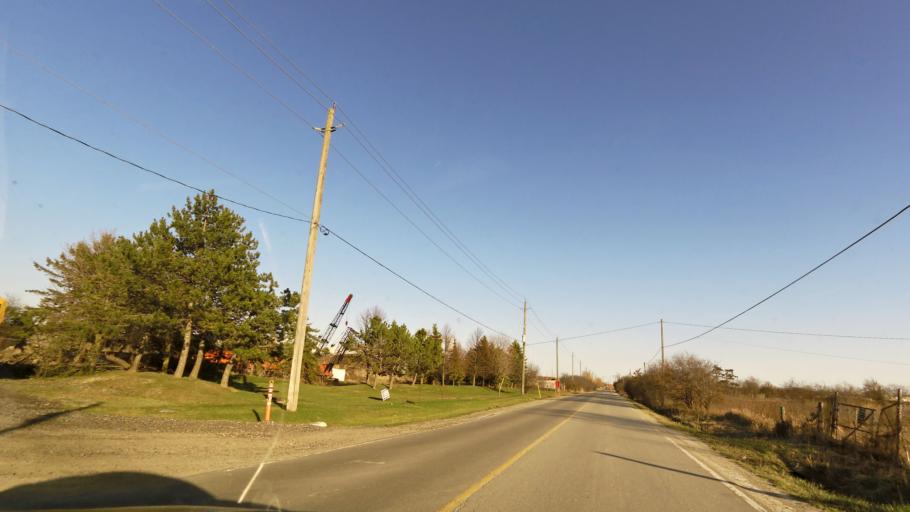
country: CA
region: Ontario
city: Brampton
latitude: 43.8225
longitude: -79.6836
